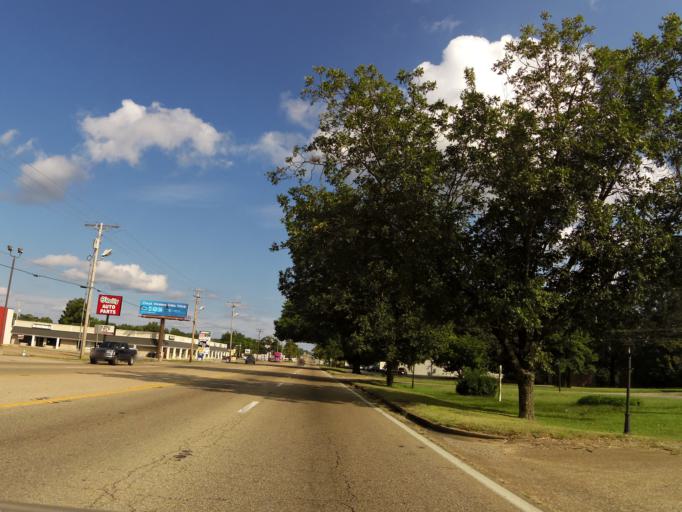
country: US
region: Mississippi
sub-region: Alcorn County
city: Corinth
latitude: 34.9179
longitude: -88.5091
